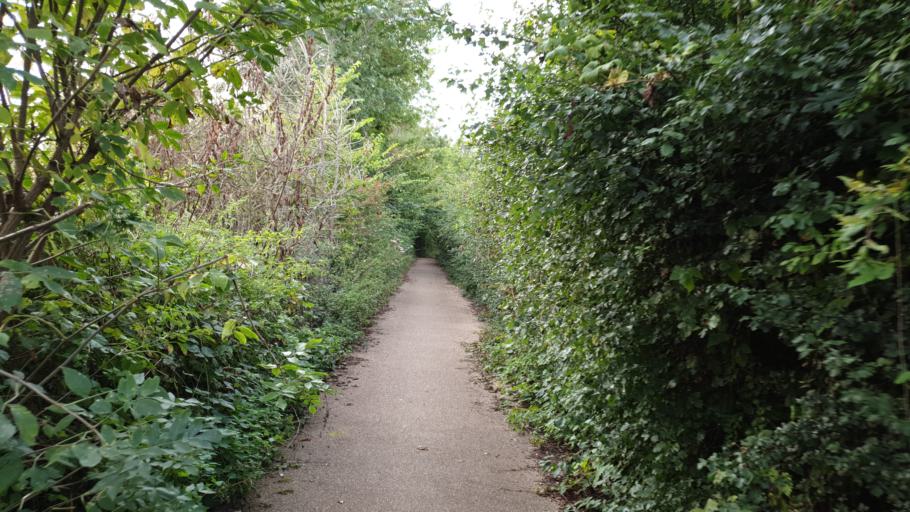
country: GB
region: England
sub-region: Wiltshire
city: Minety
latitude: 51.6494
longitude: -1.9691
